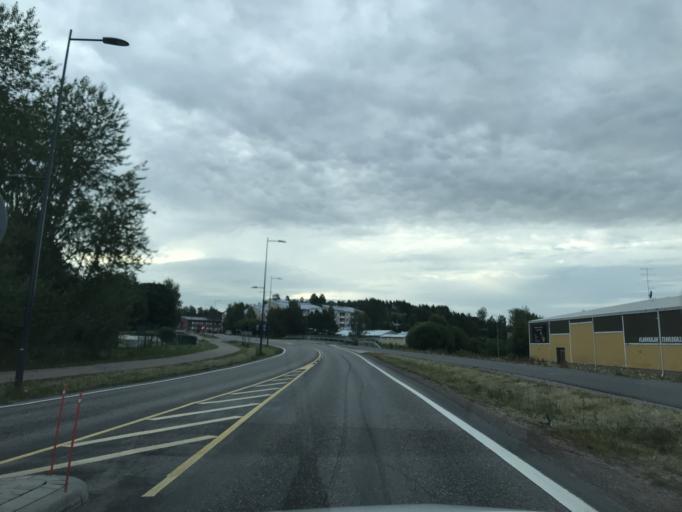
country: FI
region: Uusimaa
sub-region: Helsinki
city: Nurmijaervi
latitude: 60.3792
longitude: 24.7392
